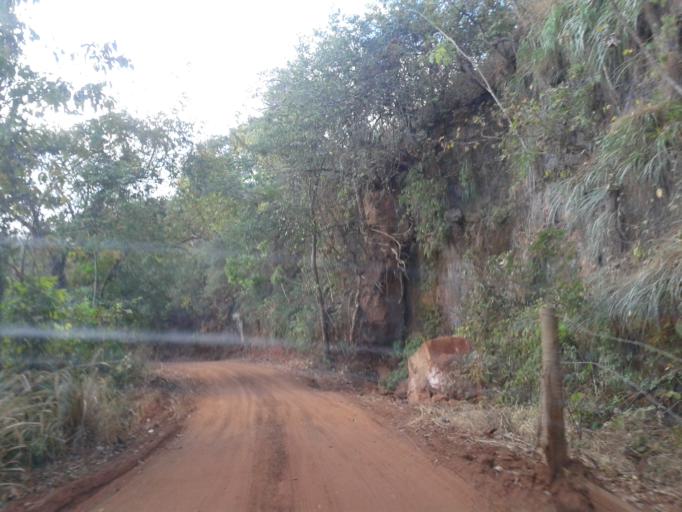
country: BR
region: Minas Gerais
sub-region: Santa Vitoria
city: Santa Vitoria
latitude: -19.1967
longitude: -49.8816
